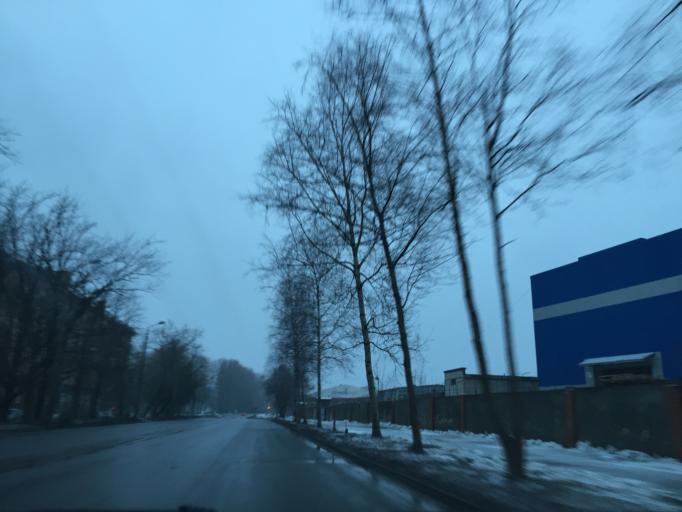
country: LV
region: Riga
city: Riga
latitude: 56.9682
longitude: 24.0722
